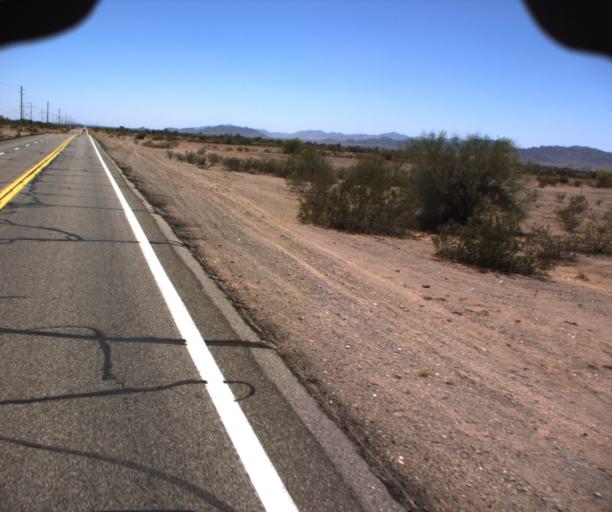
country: US
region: Arizona
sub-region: La Paz County
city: Quartzsite
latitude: 33.7796
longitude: -114.2170
